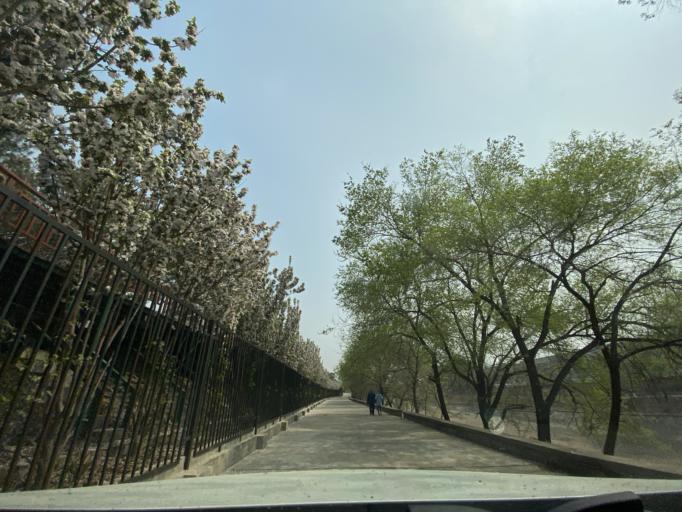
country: CN
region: Beijing
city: Sijiqing
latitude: 39.9398
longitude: 116.2485
